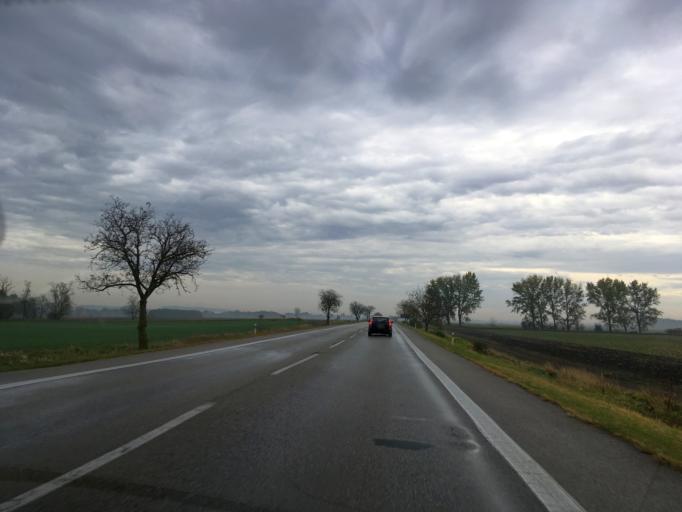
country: SK
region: Nitriansky
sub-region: Okres Komarno
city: Hurbanovo
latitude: 47.8304
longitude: 18.1730
